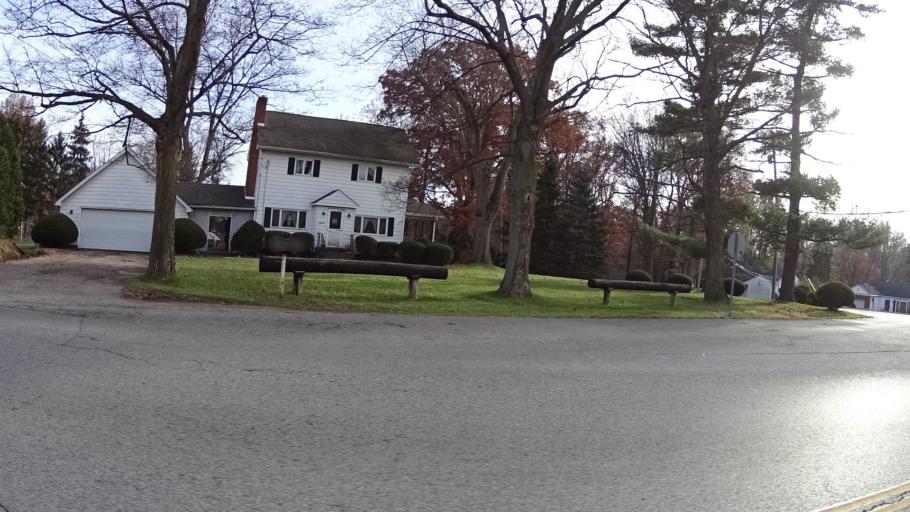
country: US
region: Ohio
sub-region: Lorain County
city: Elyria
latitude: 41.3416
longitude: -82.0881
